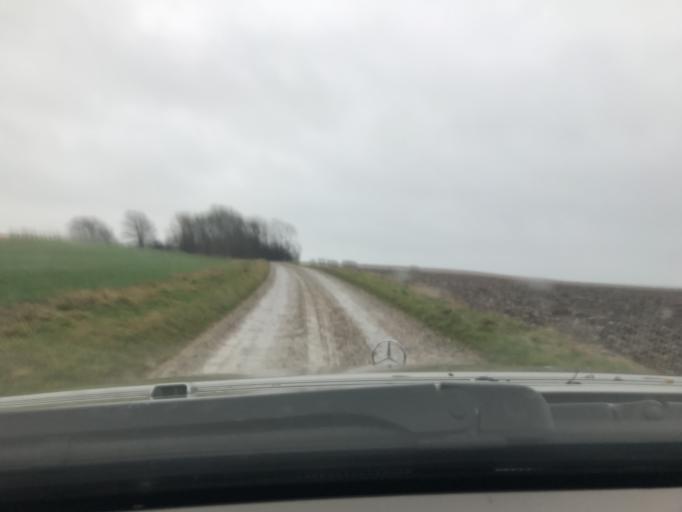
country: DK
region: South Denmark
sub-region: Sonderborg Kommune
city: Horuphav
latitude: 54.8784
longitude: 9.8703
